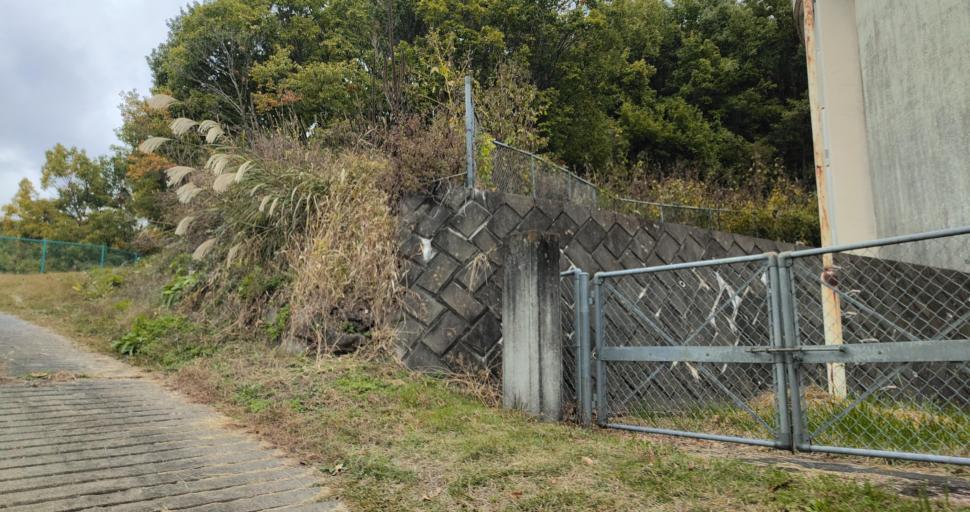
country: JP
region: Nagano
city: Komoro
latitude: 36.3636
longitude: 138.3842
